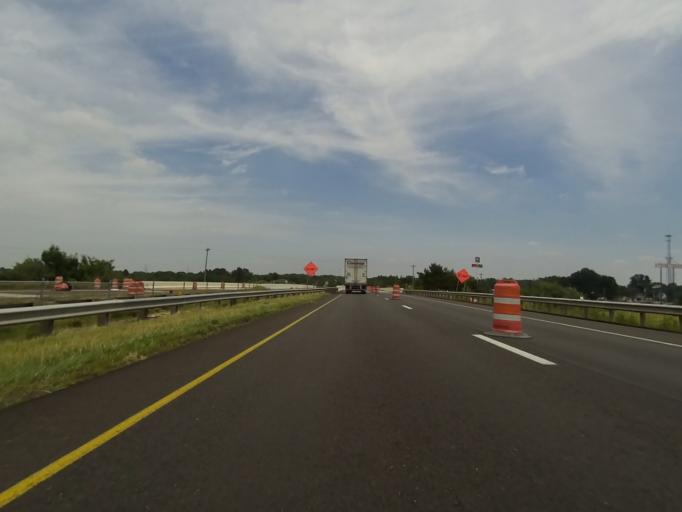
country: US
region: Ohio
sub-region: Portage County
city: Ravenna
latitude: 41.1057
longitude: -81.1577
